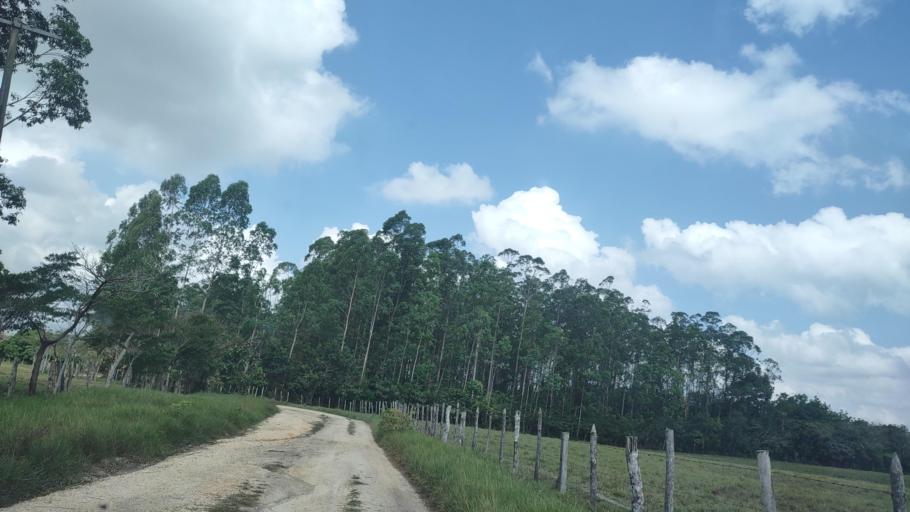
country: MX
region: Veracruz
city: Las Choapas
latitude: 17.9456
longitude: -94.0991
